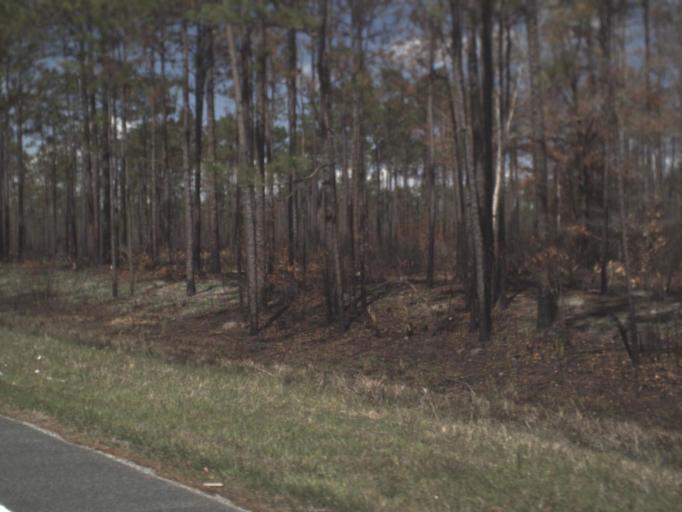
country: US
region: Florida
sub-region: Gadsden County
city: Midway
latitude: 30.3633
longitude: -84.5376
